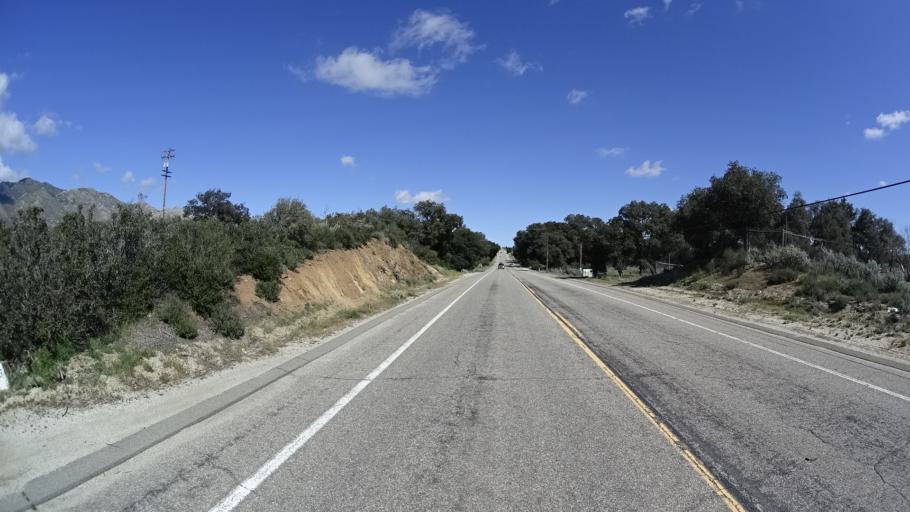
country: US
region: California
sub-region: San Diego County
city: Julian
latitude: 33.2103
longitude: -116.5395
